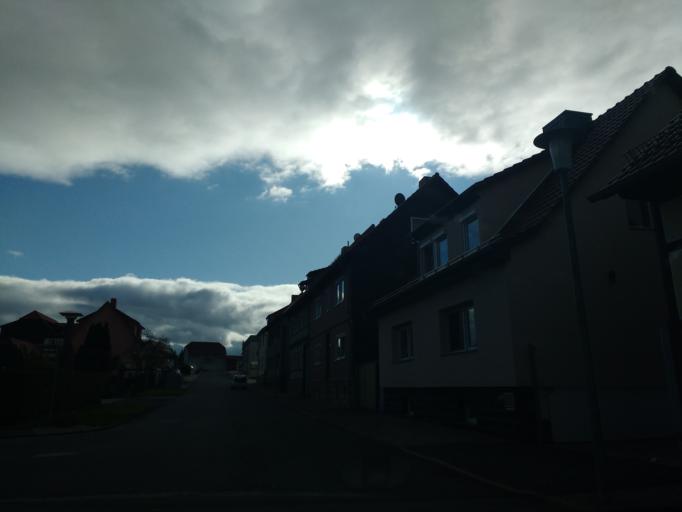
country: DE
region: Thuringia
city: Breitenworbis
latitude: 51.4120
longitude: 10.4251
